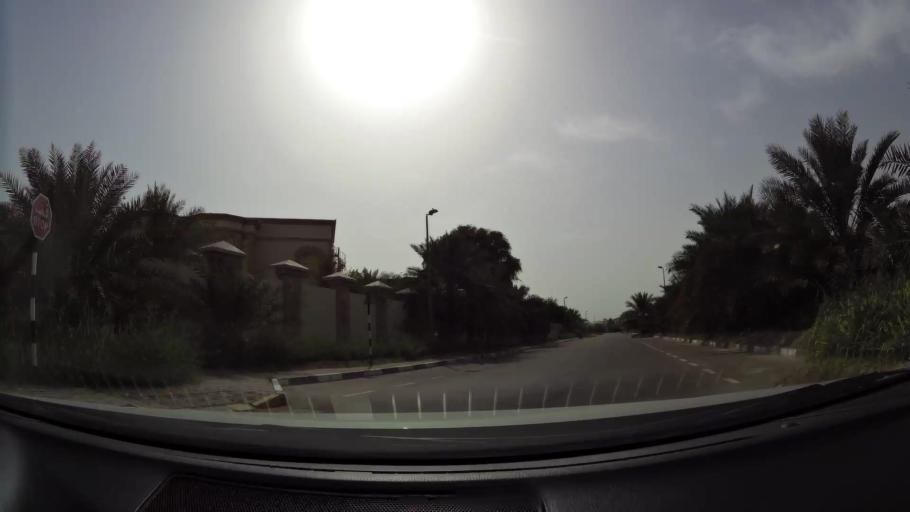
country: AE
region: Abu Dhabi
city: Al Ain
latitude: 24.1480
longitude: 55.7056
